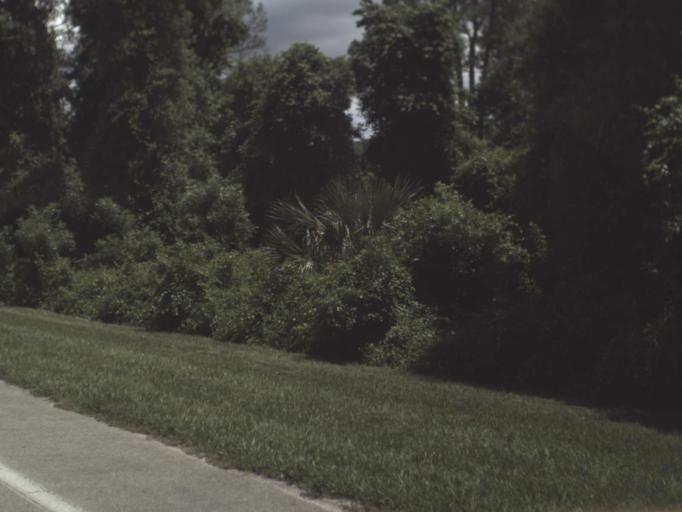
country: US
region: Florida
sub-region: Putnam County
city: Crescent City
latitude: 29.3984
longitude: -81.5091
